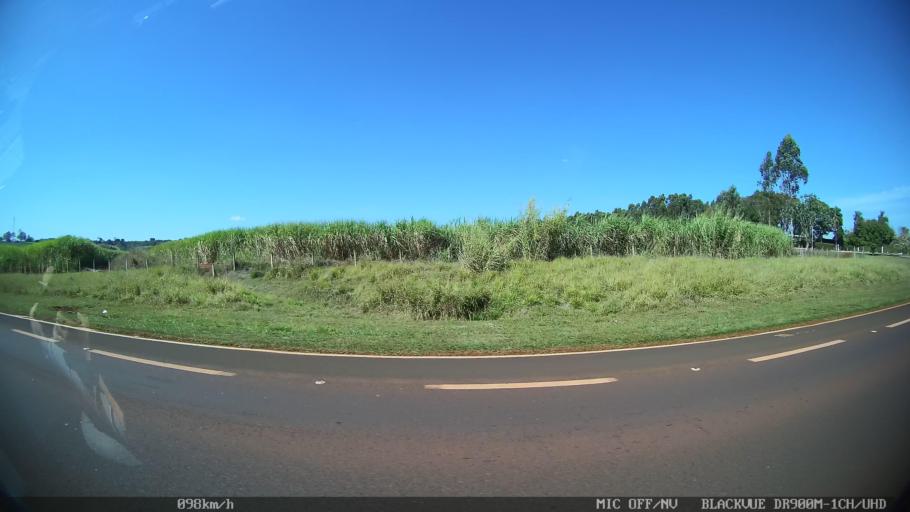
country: BR
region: Sao Paulo
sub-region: Franca
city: Franca
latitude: -20.6472
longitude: -47.4820
